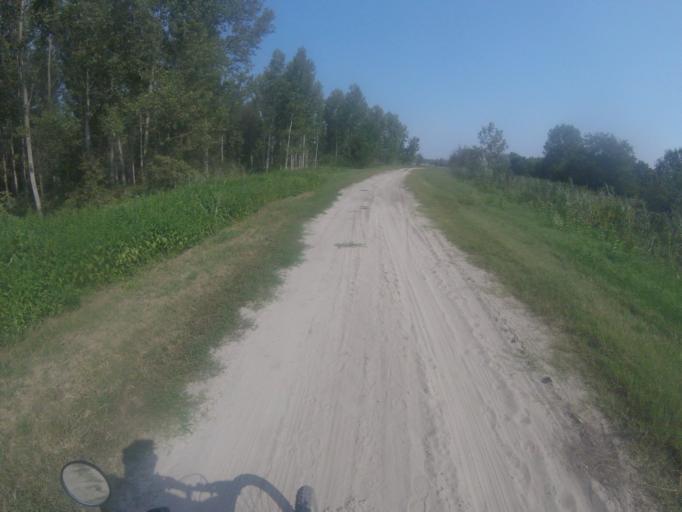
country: HU
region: Bacs-Kiskun
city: Ersekcsanad
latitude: 46.2490
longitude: 18.9689
